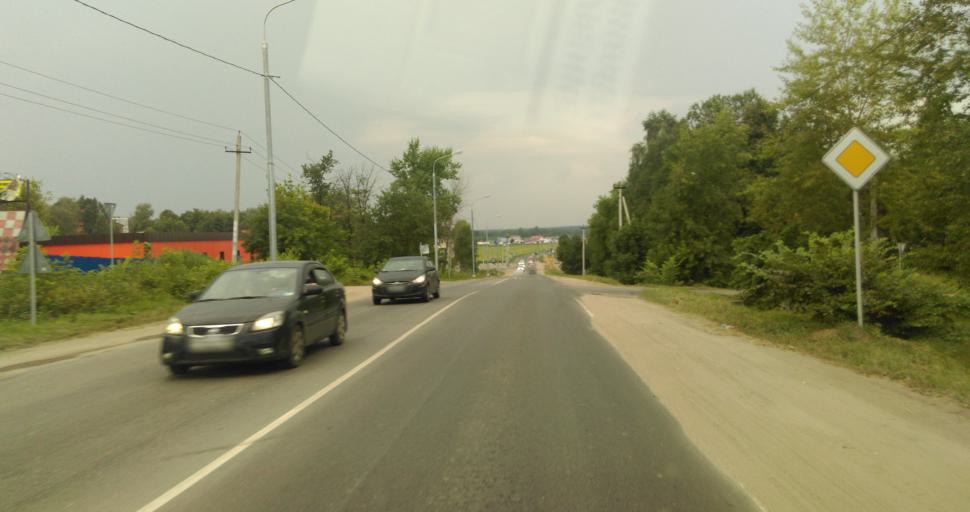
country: RU
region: Moskovskaya
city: Zhitnevo
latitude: 55.3432
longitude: 37.9044
